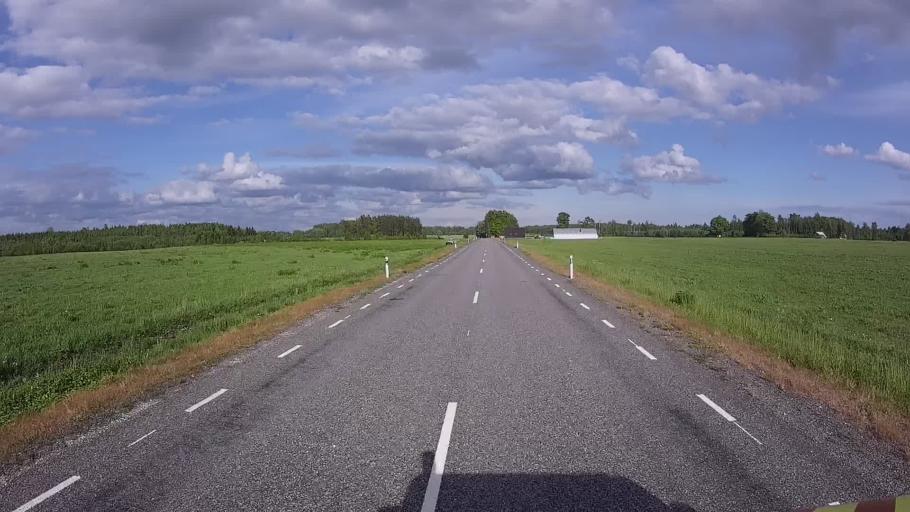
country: EE
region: Jogevamaa
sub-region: Mustvee linn
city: Mustvee
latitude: 59.0255
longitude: 27.0134
